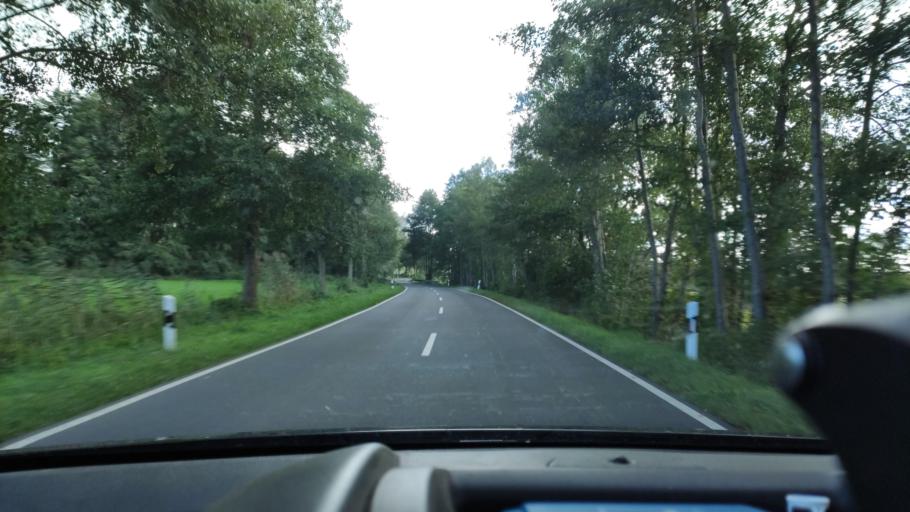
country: DE
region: Mecklenburg-Vorpommern
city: Butzow
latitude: 53.8070
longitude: 11.9562
